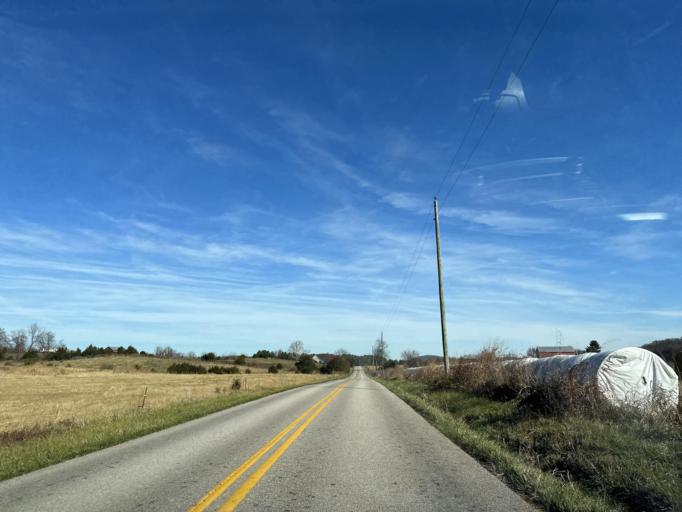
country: US
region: Virginia
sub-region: Augusta County
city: Fishersville
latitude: 38.1417
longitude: -78.9370
